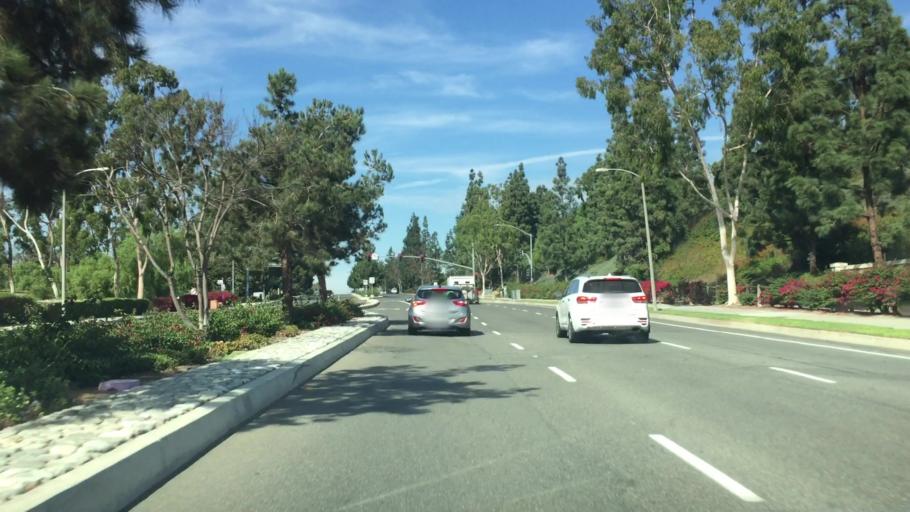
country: US
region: California
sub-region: Orange County
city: Laguna Niguel
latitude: 33.5285
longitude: -117.6851
